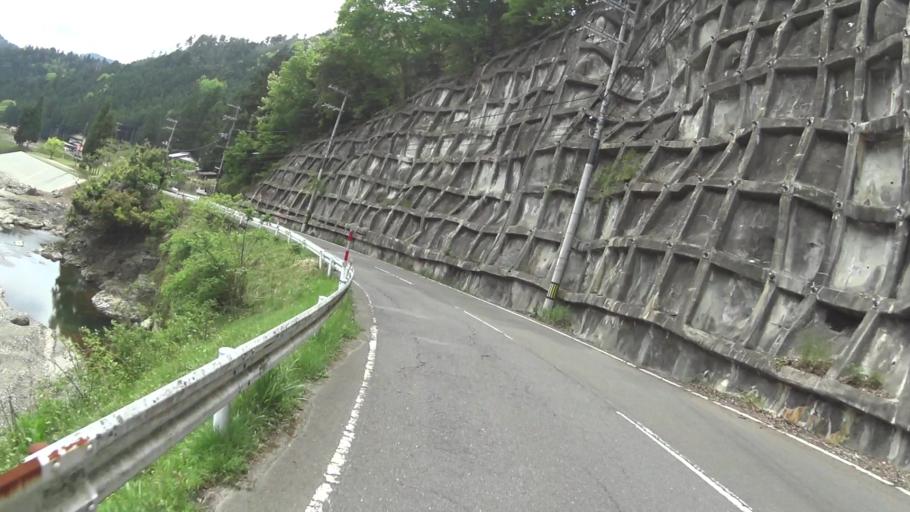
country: JP
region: Kyoto
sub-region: Kyoto-shi
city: Kamigyo-ku
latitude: 35.2029
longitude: 135.7121
